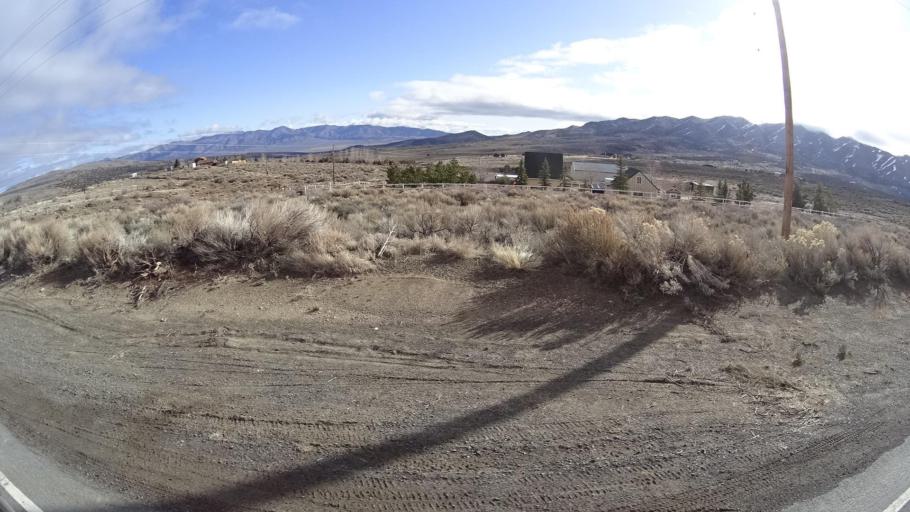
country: US
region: Nevada
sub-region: Washoe County
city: Cold Springs
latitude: 39.7918
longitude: -119.9004
